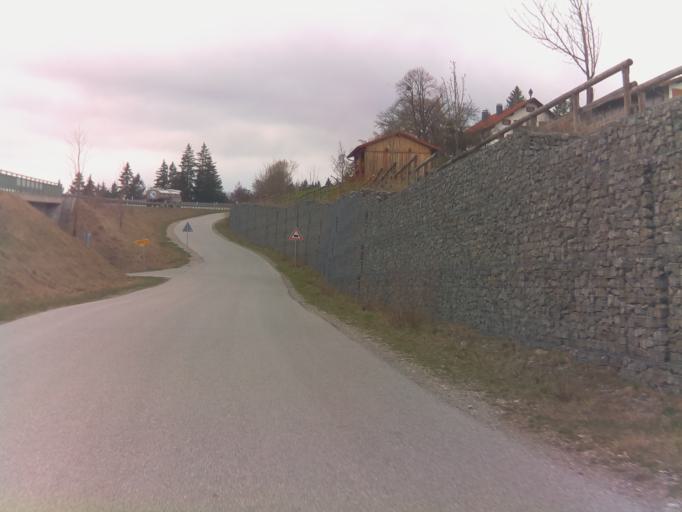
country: DE
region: Bavaria
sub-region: Upper Bavaria
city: Peissenberg
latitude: 47.7810
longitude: 11.0397
